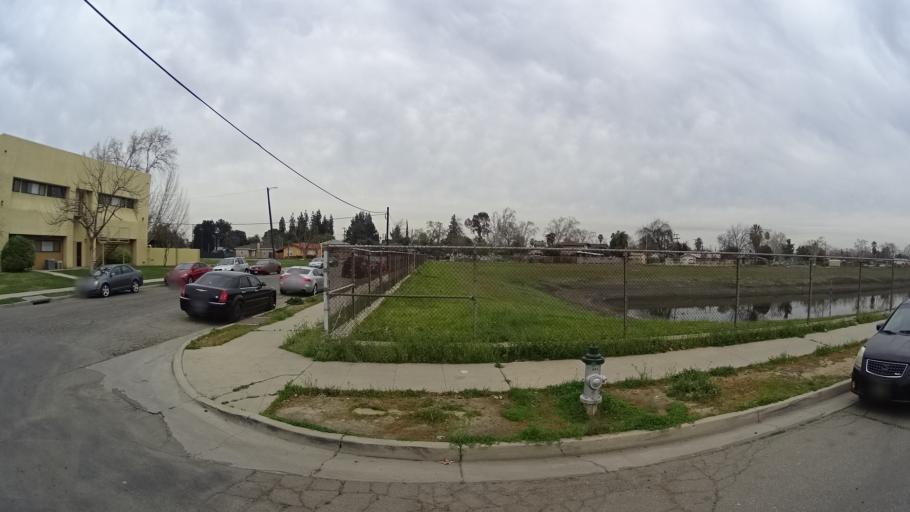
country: US
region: California
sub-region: Fresno County
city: Fresno
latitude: 36.7339
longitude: -119.7755
